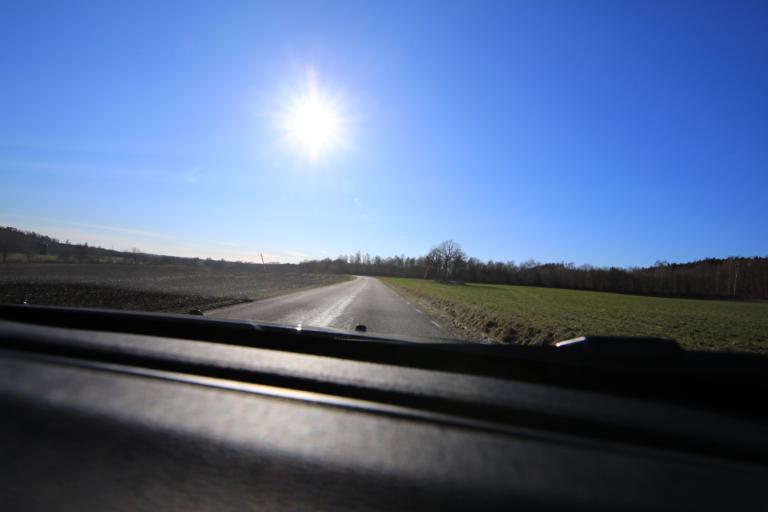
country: SE
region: Halland
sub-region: Varbergs Kommun
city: Tvaaker
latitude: 57.0662
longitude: 12.4648
